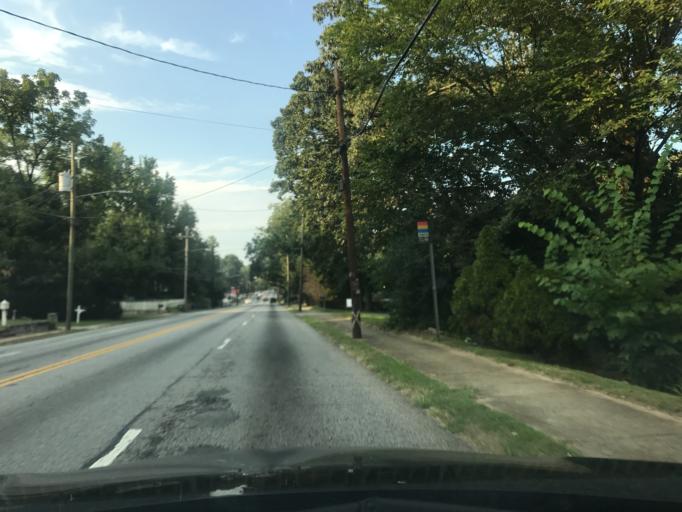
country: US
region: Georgia
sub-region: Fulton County
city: Atlanta
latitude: 33.7299
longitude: -84.3493
